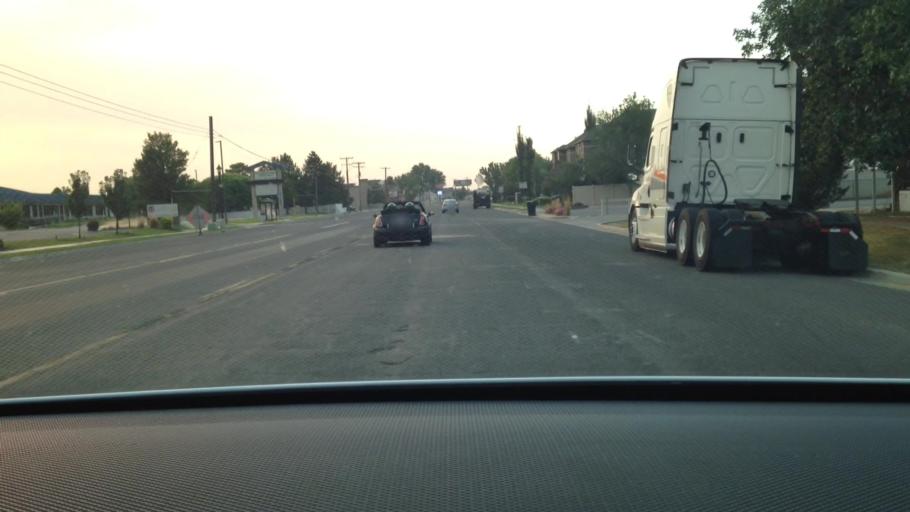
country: US
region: Utah
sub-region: Davis County
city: Kaysville
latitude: 41.0459
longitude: -111.9523
